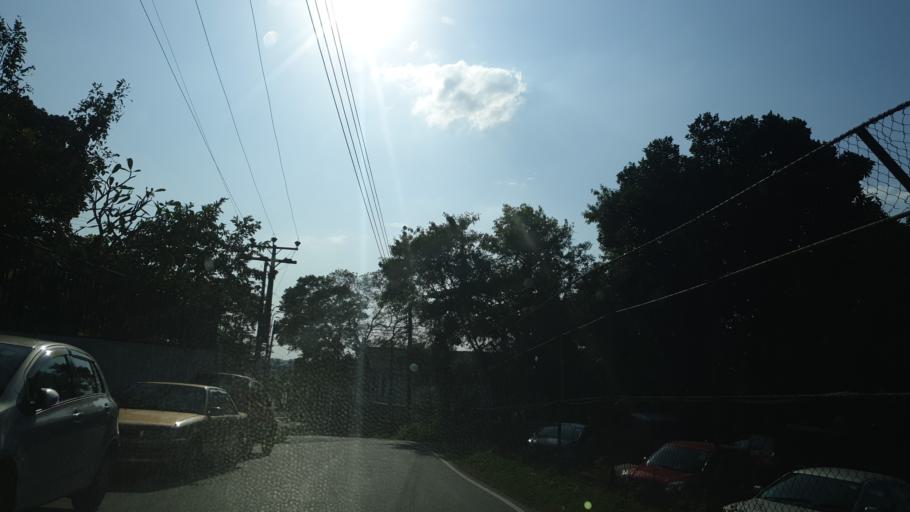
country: LK
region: Western
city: Battaramulla South
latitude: 6.8840
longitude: 79.9411
